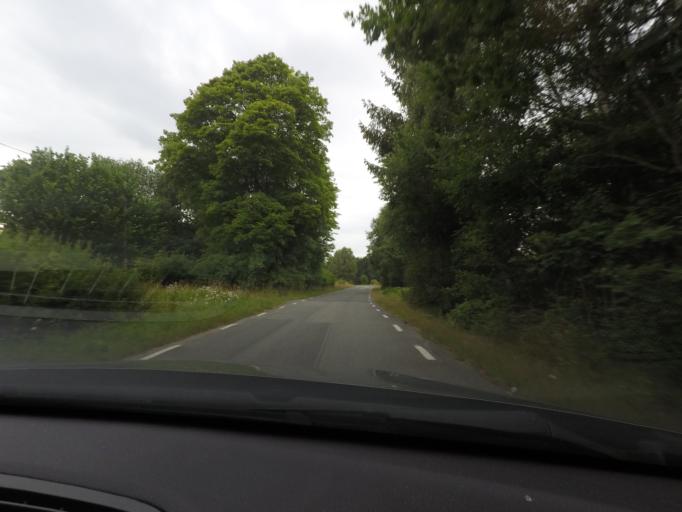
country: SE
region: Kronoberg
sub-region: Markaryds Kommun
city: Markaryd
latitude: 56.4156
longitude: 13.6965
